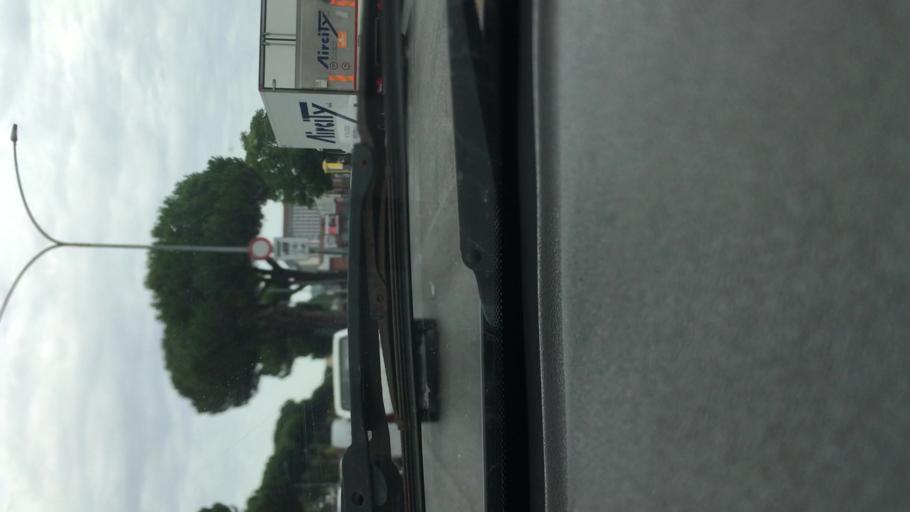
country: IT
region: Latium
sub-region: Citta metropolitana di Roma Capitale
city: Rome
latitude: 41.8543
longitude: 12.4905
